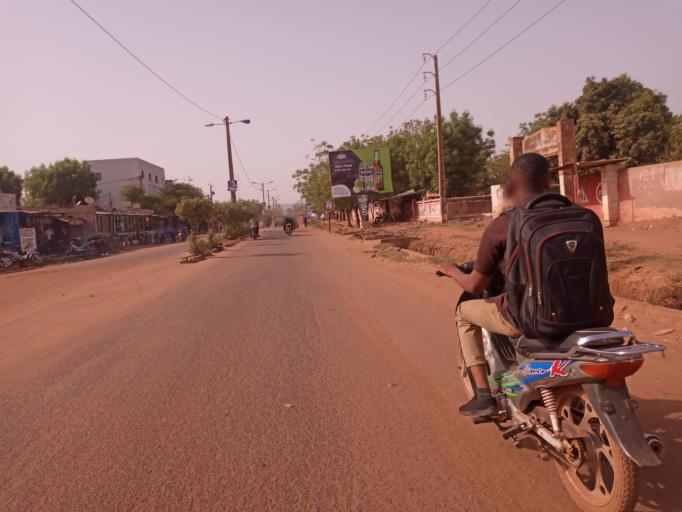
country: ML
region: Bamako
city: Bamako
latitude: 12.6667
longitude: -7.9418
